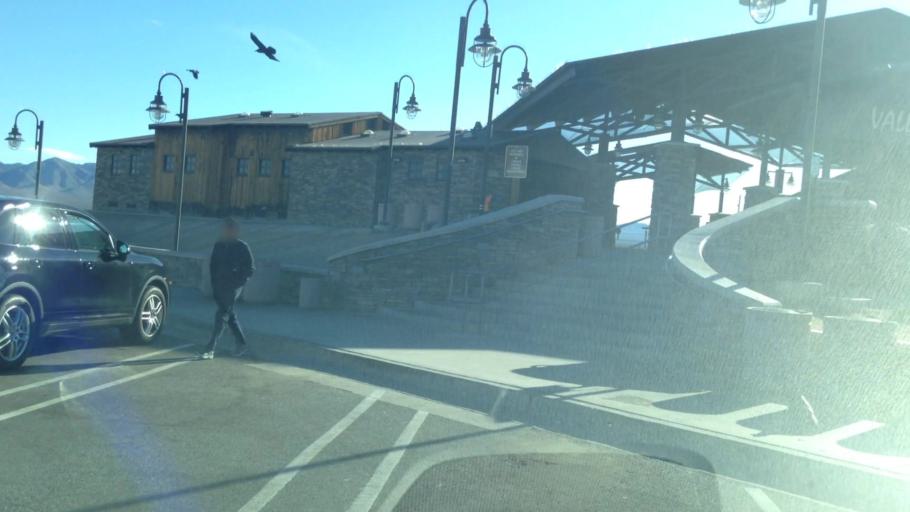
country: US
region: Nevada
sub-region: Clark County
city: Sandy Valley
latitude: 35.4341
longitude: -115.6997
